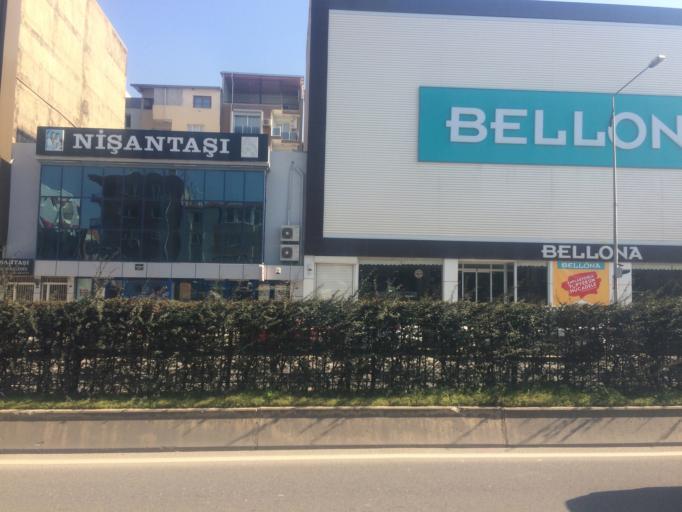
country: TR
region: Izmir
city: Karsiyaka
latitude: 38.4990
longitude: 27.0565
